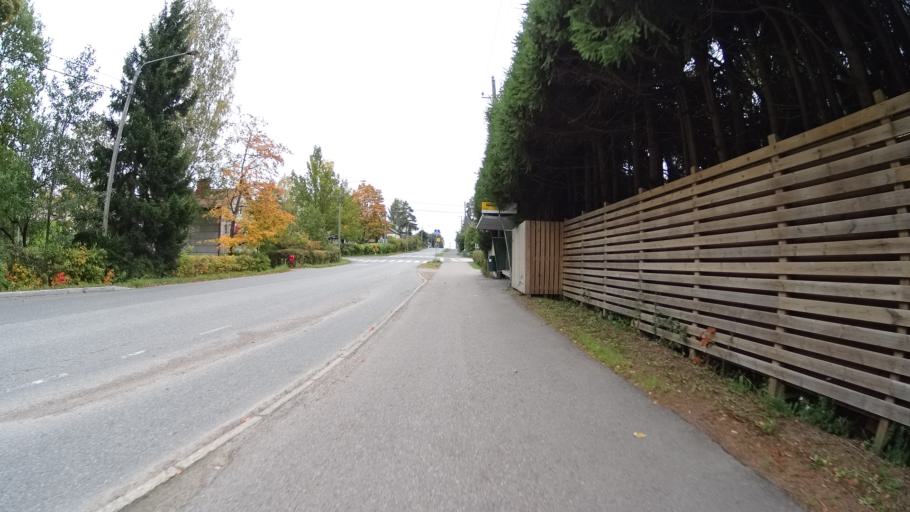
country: FI
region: Uusimaa
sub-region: Helsinki
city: Kilo
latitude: 60.2414
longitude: 24.8086
